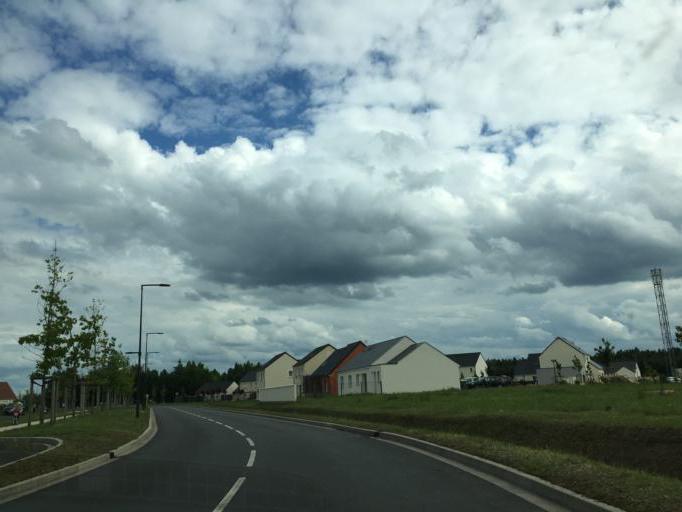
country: FR
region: Centre
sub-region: Departement du Loiret
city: Saint-Pryve-Saint-Mesmin
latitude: 47.8636
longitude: 1.8733
